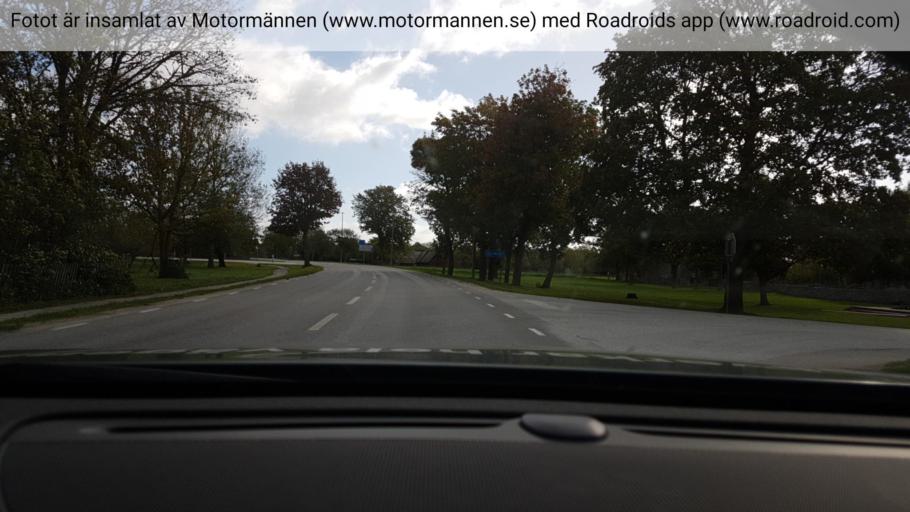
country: SE
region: Gotland
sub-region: Gotland
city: Slite
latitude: 57.8546
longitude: 19.0226
